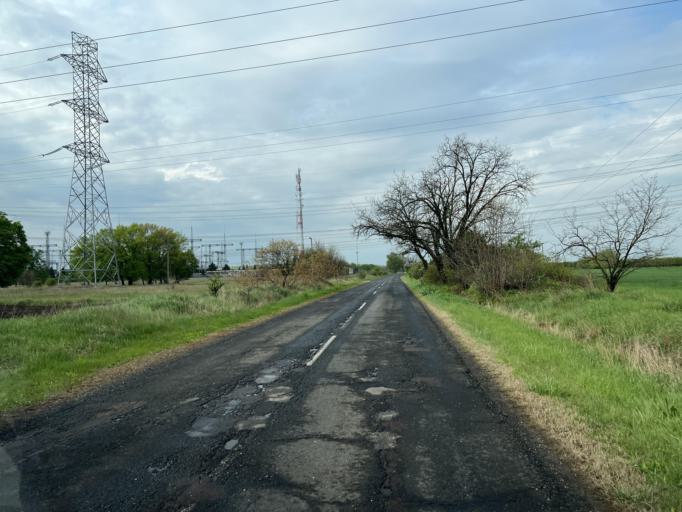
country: HU
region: Pest
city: Albertirsa
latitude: 47.2301
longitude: 19.5822
